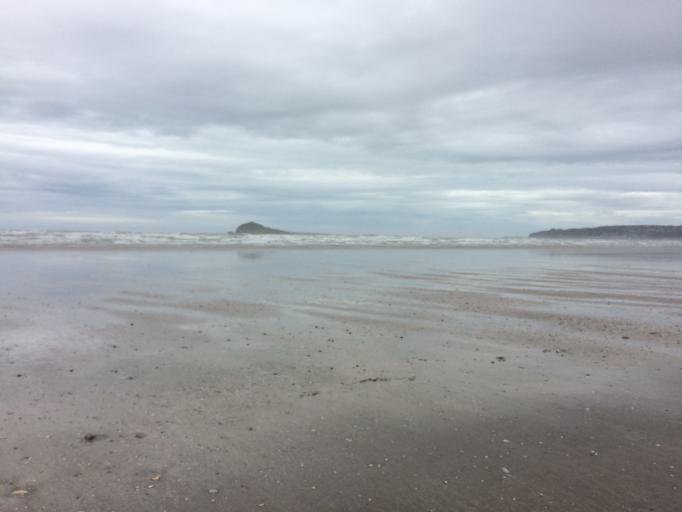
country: IE
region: Leinster
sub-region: Fingal County
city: Baldoyle
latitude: 53.4099
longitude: -6.1151
